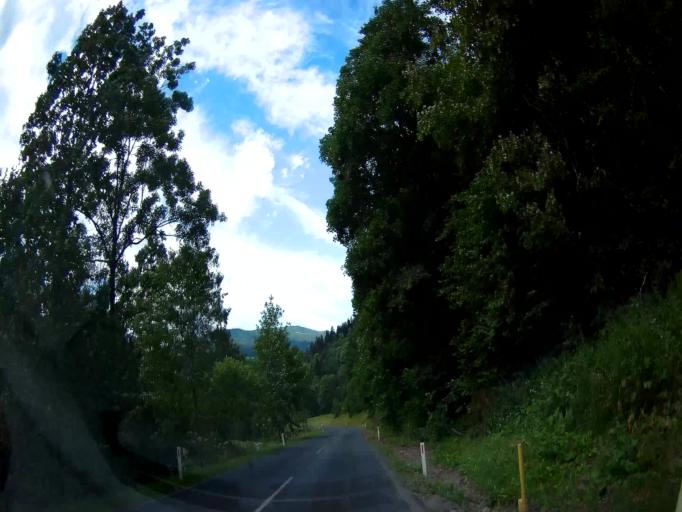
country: AT
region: Styria
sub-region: Politischer Bezirk Murau
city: Stadl an der Mur
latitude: 47.0690
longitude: 13.9853
